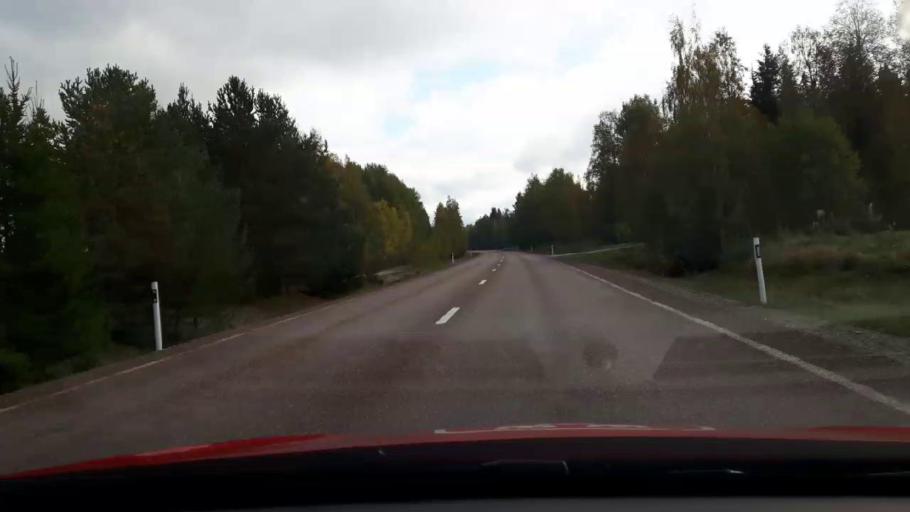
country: SE
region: Gaevleborg
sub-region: Ljusdals Kommun
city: Jaervsoe
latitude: 61.6464
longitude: 16.2036
